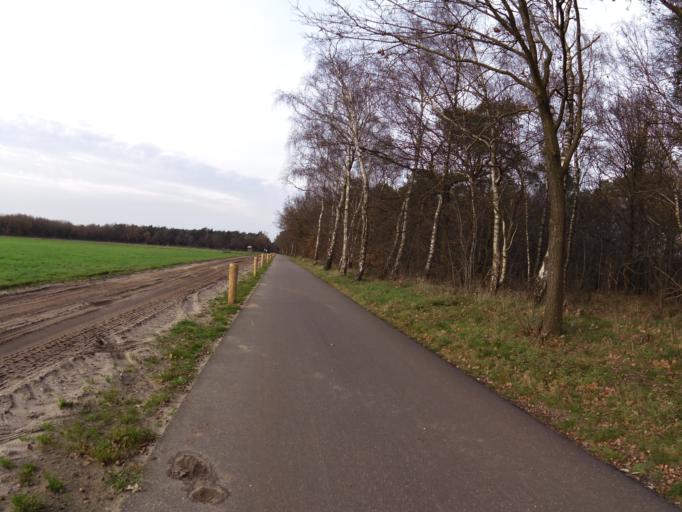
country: NL
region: North Brabant
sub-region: Gemeente Uden
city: Uden
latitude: 51.6996
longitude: 5.5991
